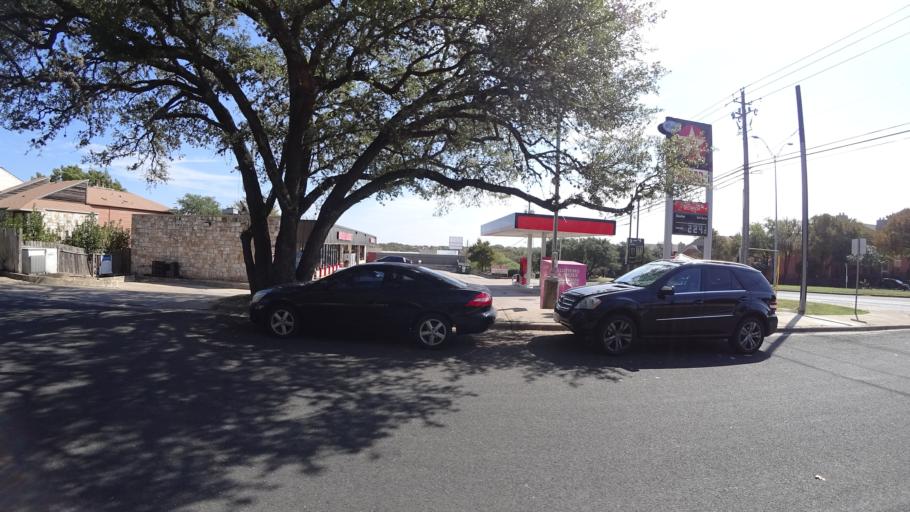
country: US
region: Texas
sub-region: Travis County
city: Shady Hollow
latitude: 30.2084
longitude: -97.8178
